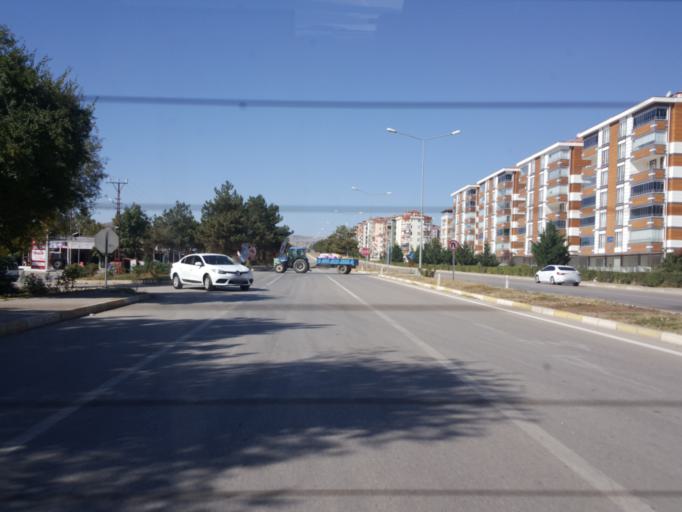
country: TR
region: Tokat
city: Zile
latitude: 40.2925
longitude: 35.8797
